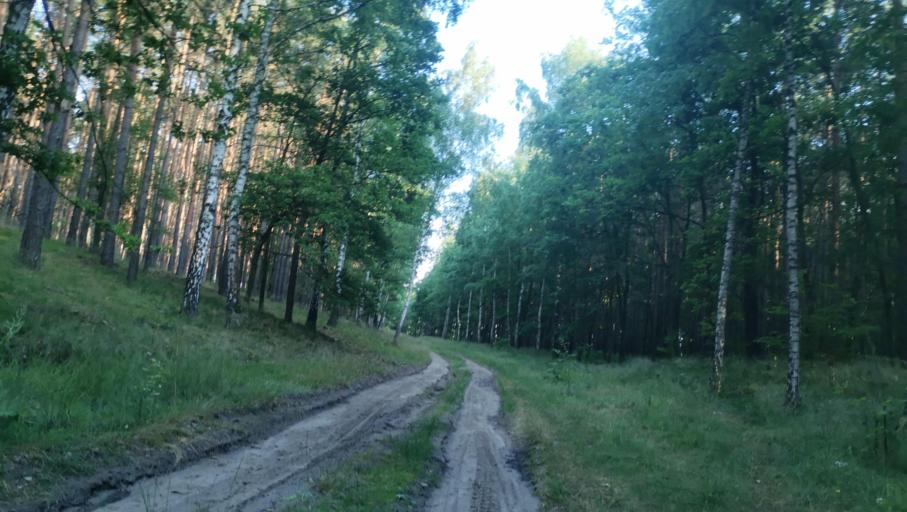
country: PL
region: Greater Poland Voivodeship
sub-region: Powiat jarocinski
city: Witaszyce
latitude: 51.9809
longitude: 17.5450
